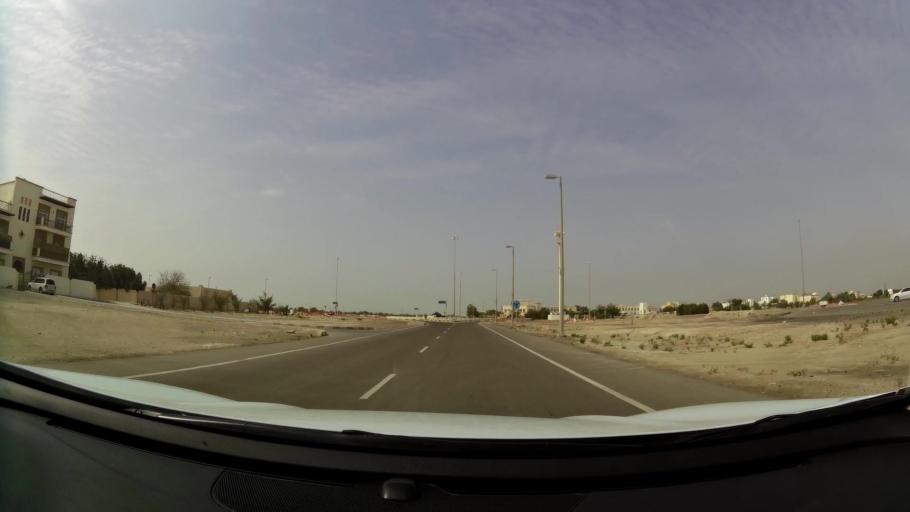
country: AE
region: Abu Dhabi
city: Abu Dhabi
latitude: 24.5370
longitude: 54.6729
